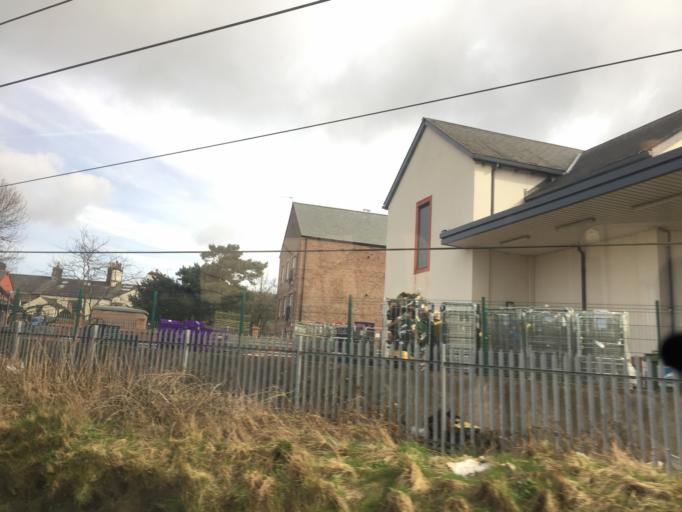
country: GB
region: England
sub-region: Cumbria
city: Penrith
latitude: 54.6649
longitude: -2.7587
